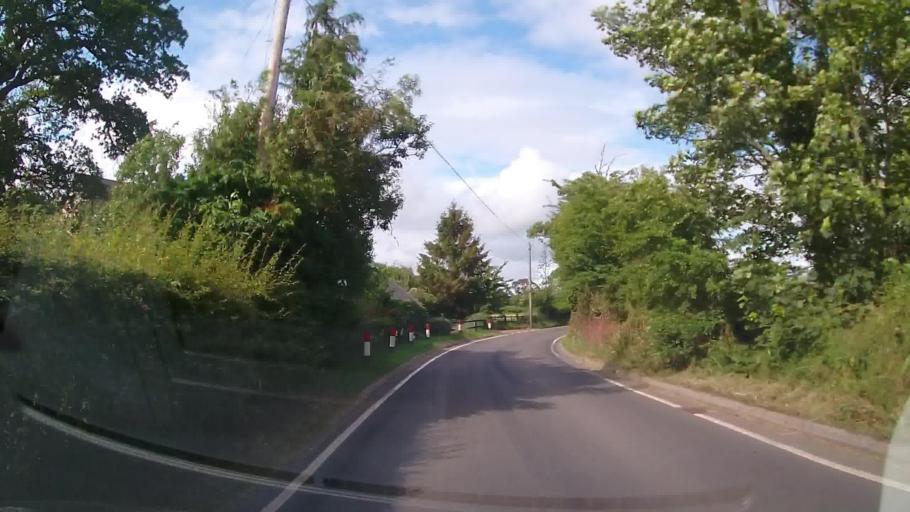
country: GB
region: England
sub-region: Shropshire
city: Petton
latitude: 52.8546
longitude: -2.7931
